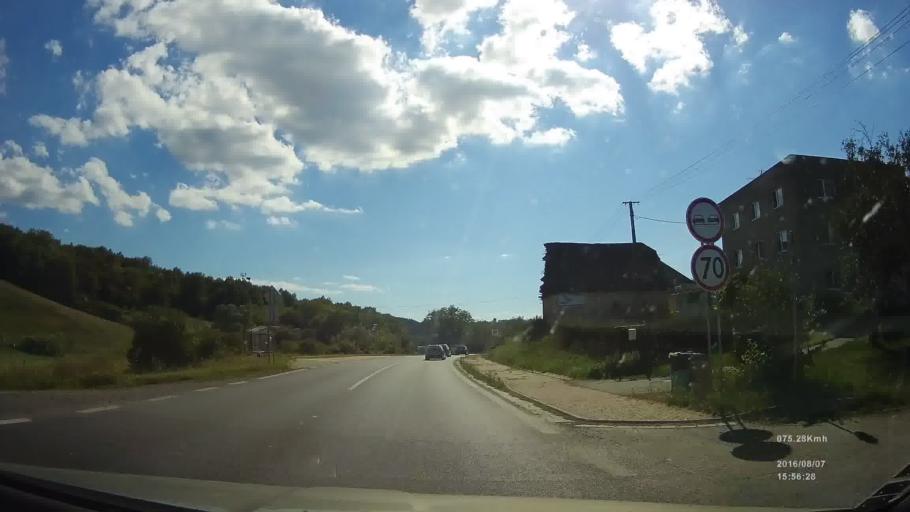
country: SK
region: Presovsky
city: Giraltovce
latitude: 49.0664
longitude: 21.4243
